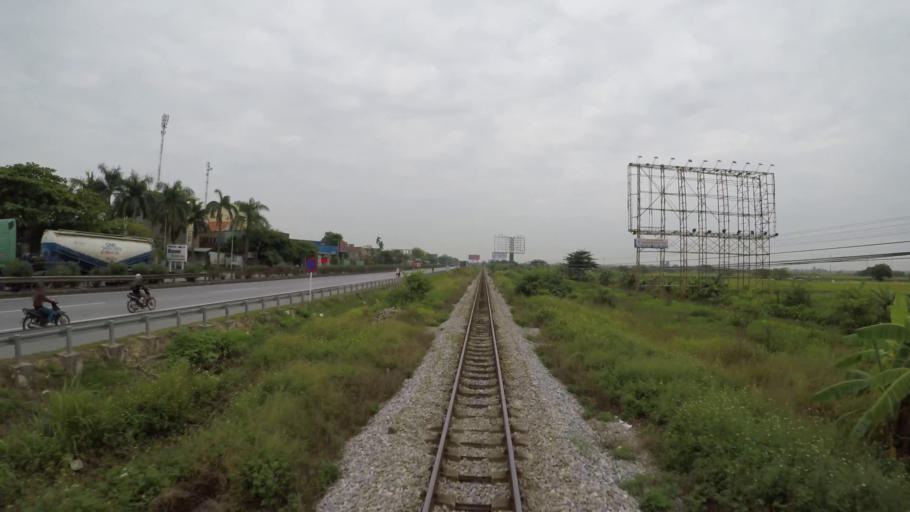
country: VN
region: Hai Duong
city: Phu Thai
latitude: 20.9379
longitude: 106.5482
